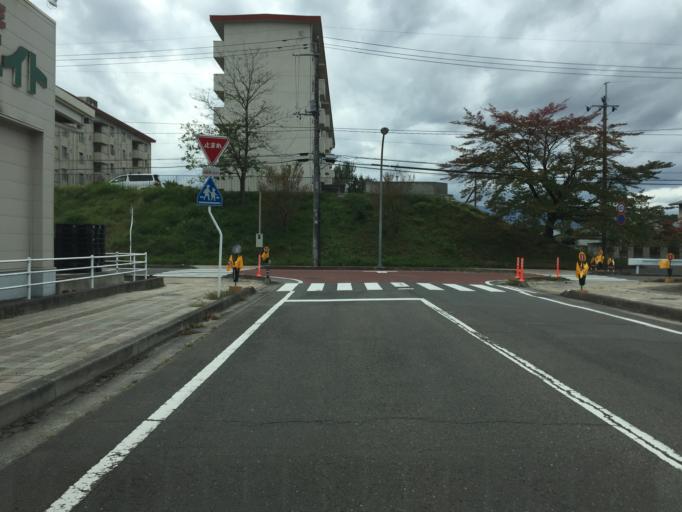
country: JP
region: Fukushima
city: Fukushima-shi
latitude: 37.6988
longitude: 140.4704
